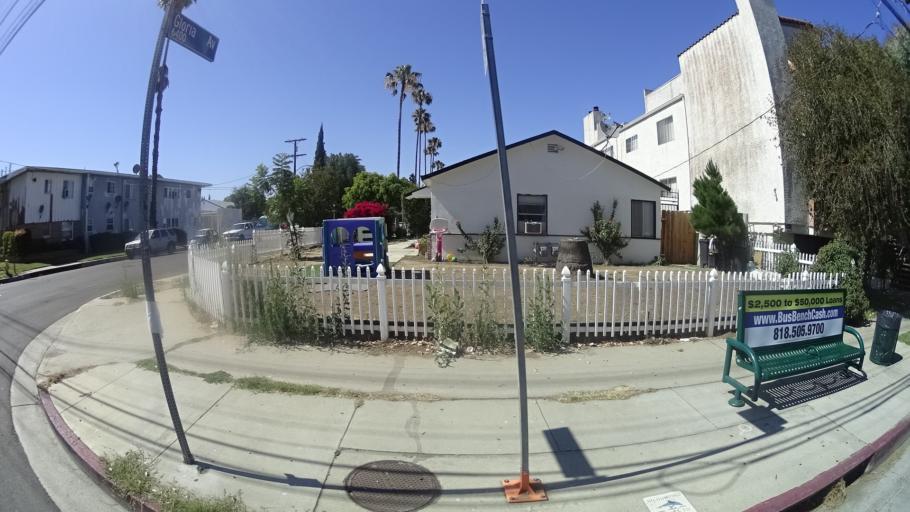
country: US
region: California
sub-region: Los Angeles County
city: Van Nuys
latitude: 34.1867
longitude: -118.4790
